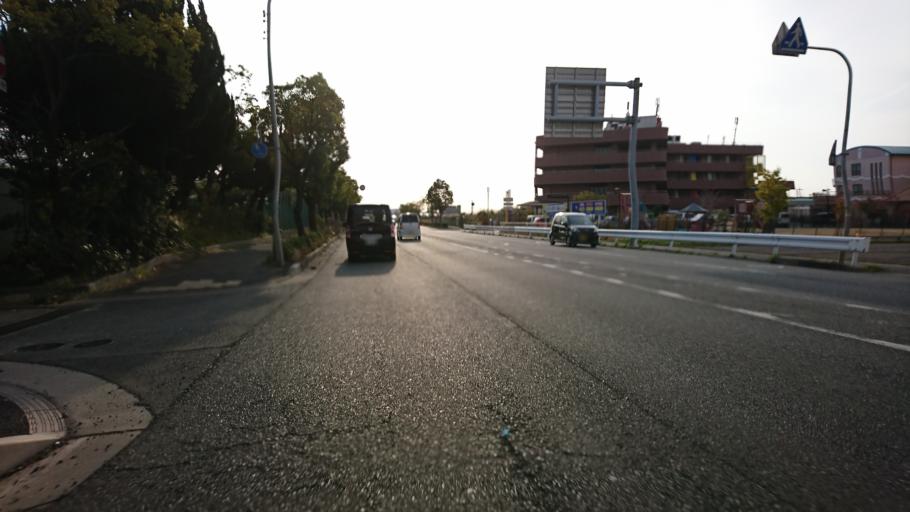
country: JP
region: Hyogo
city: Kakogawacho-honmachi
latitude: 34.7093
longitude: 134.8812
